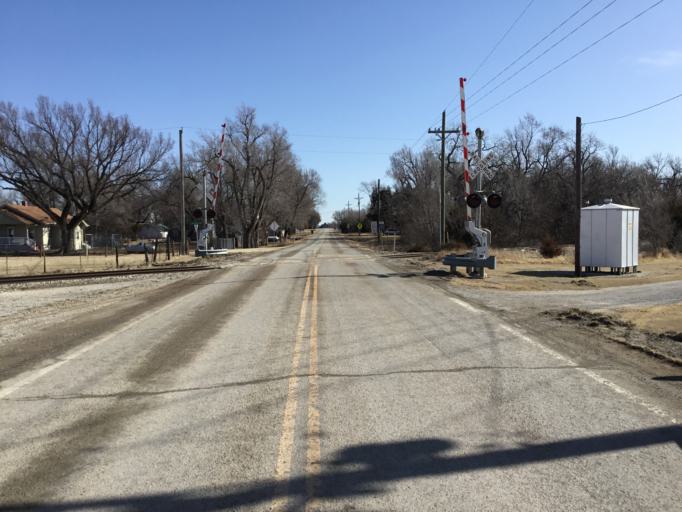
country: US
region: Kansas
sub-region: McPherson County
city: McPherson
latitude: 38.2897
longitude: -97.6250
